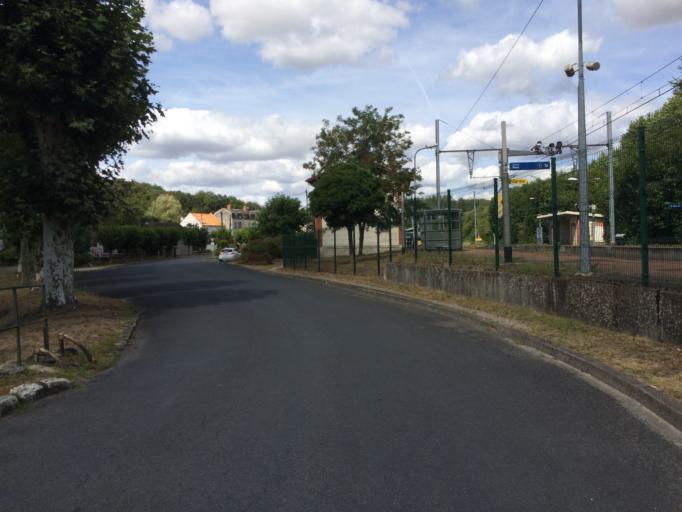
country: FR
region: Ile-de-France
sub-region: Departement de l'Essonne
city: Maisse
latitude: 48.3415
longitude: 2.3786
